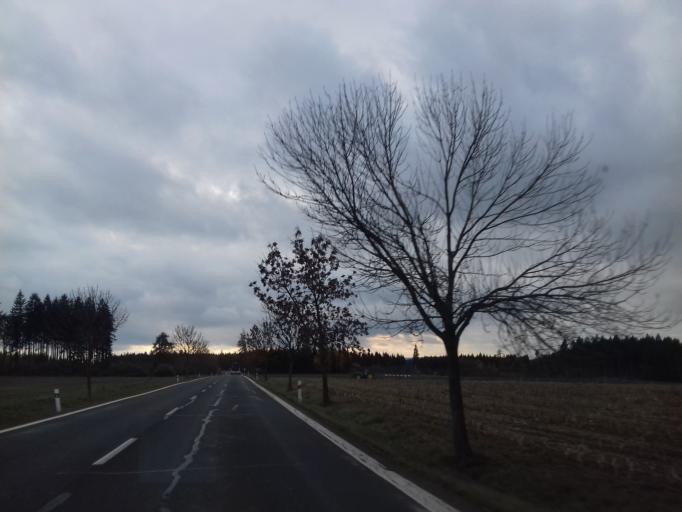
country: CZ
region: Pardubicky
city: Radimer
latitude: 49.7405
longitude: 16.3868
